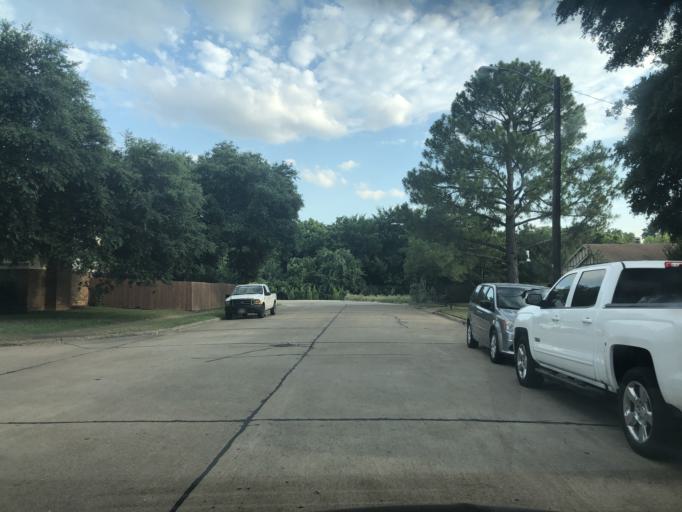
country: US
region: Texas
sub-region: Dallas County
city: Irving
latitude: 32.7918
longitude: -96.9527
